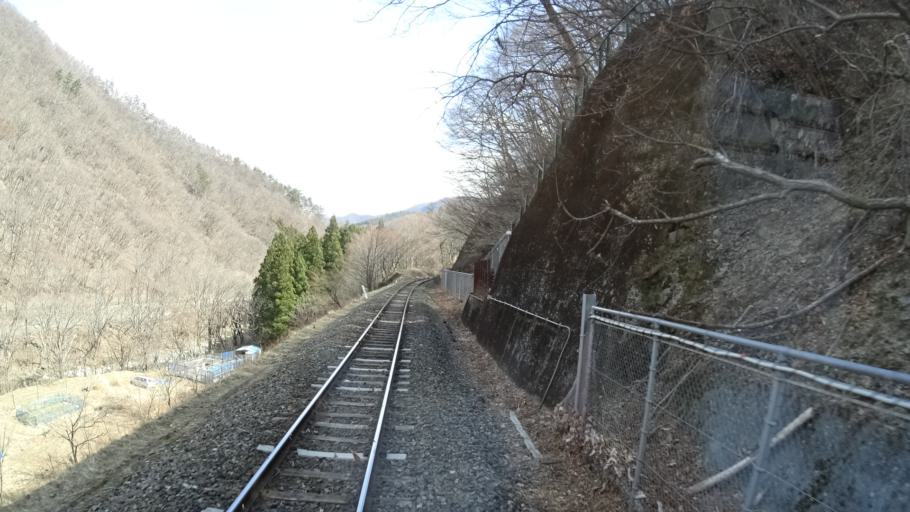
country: JP
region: Iwate
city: Kamaishi
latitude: 39.2557
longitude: 141.7357
